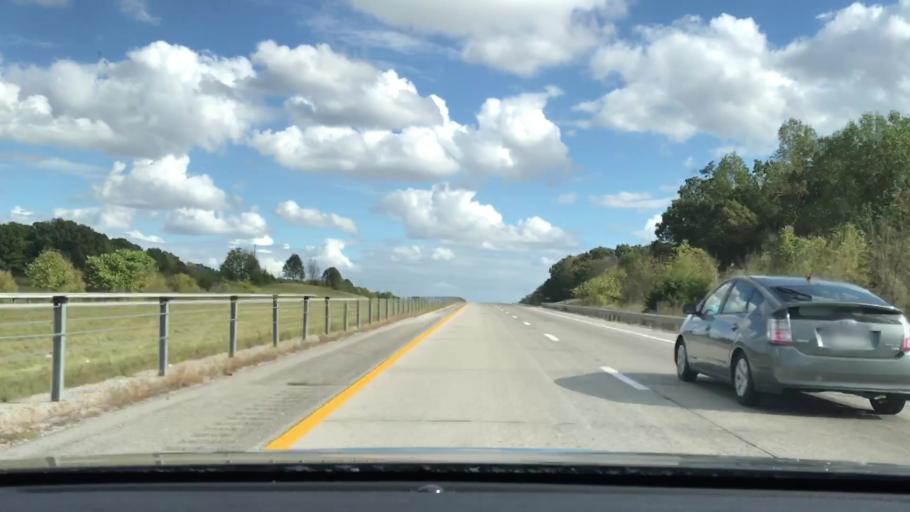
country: US
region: Kentucky
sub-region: Trigg County
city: Cadiz
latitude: 36.9333
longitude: -87.8186
